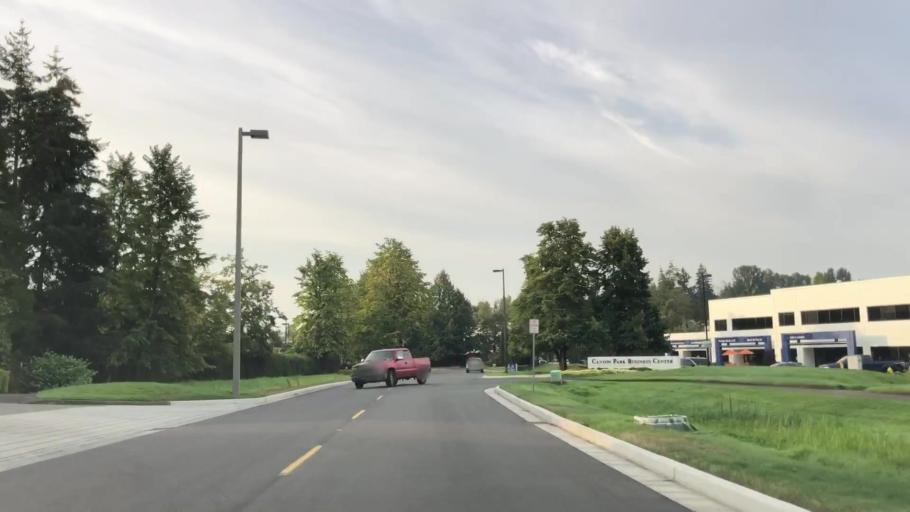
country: US
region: Washington
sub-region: King County
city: Bothell
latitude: 47.7981
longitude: -122.2055
